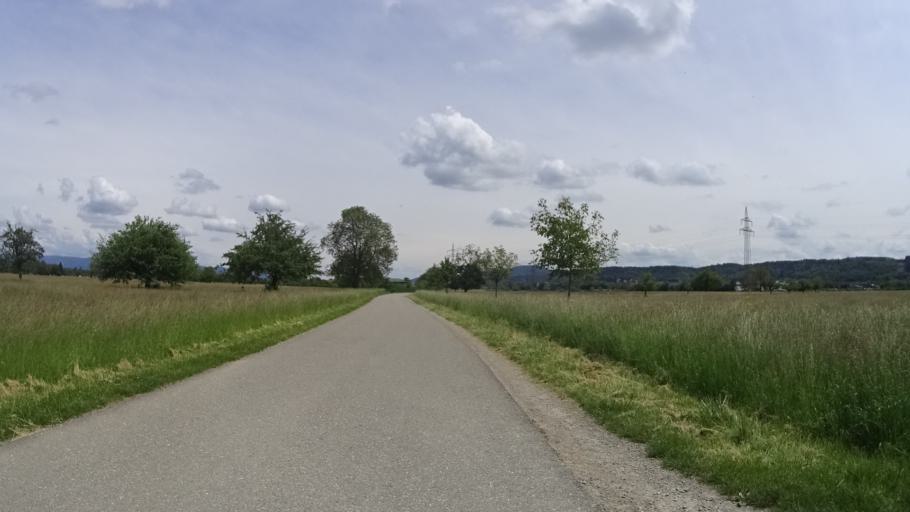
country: CH
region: Aargau
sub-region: Bezirk Rheinfelden
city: Kaiseraugst
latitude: 47.5549
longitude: 7.7458
